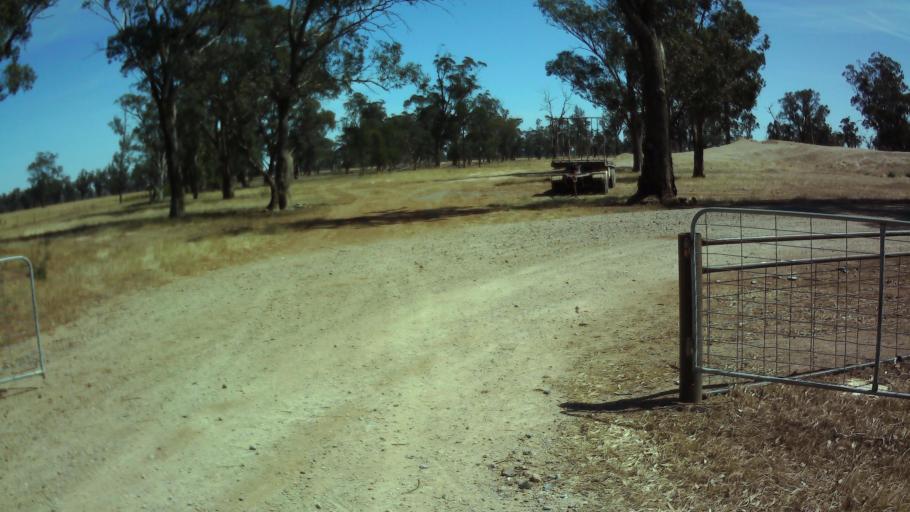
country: AU
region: New South Wales
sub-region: Weddin
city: Grenfell
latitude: -34.1147
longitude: 147.8136
